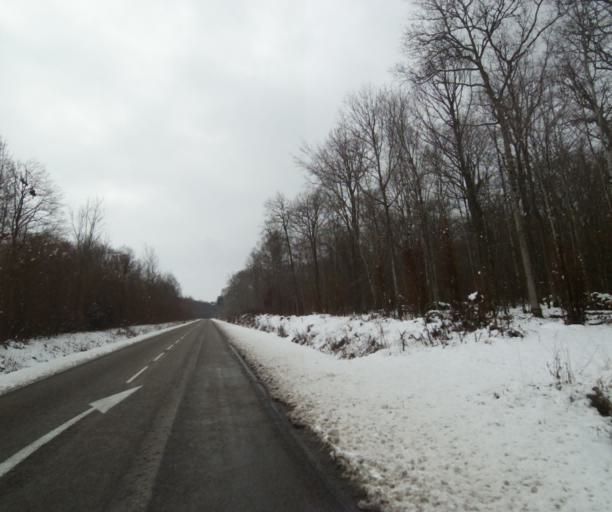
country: FR
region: Champagne-Ardenne
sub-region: Departement de la Haute-Marne
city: Laneuville-a-Remy
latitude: 48.4874
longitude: 4.8307
